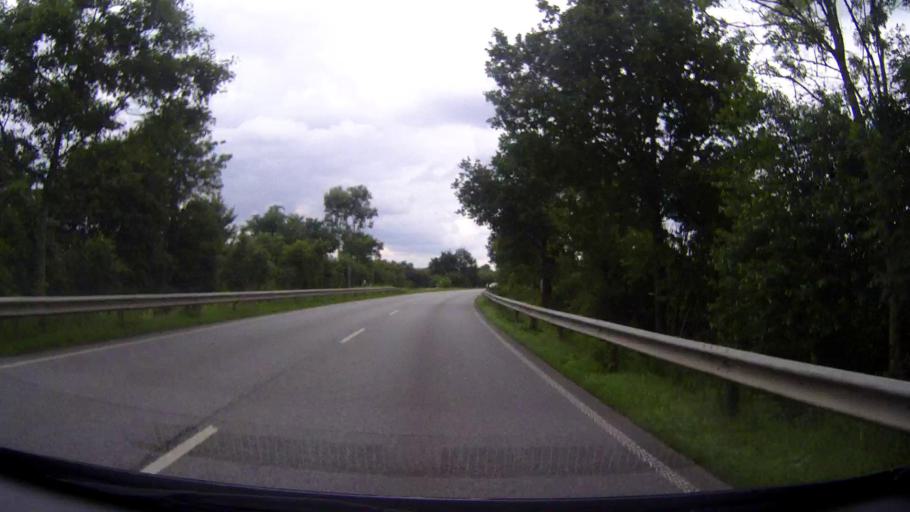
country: DE
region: Schleswig-Holstein
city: Hohenwestedt
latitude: 54.0809
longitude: 9.6547
